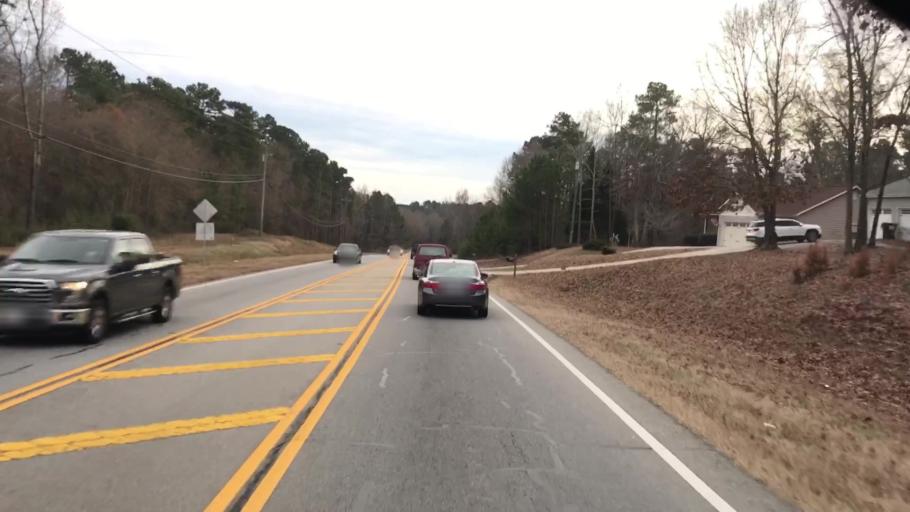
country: US
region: Georgia
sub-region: Jackson County
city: Hoschton
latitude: 34.0425
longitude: -83.7766
